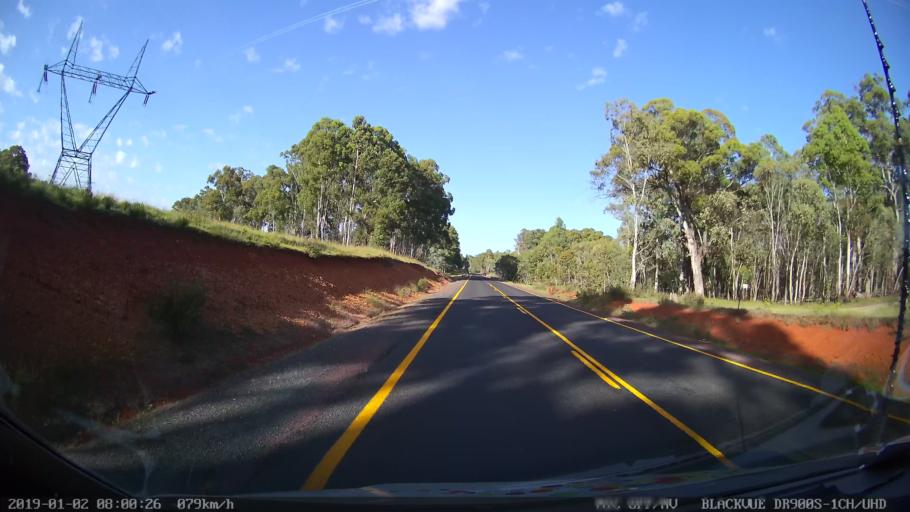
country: AU
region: New South Wales
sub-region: Tumut Shire
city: Tumut
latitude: -35.6443
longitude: 148.4455
